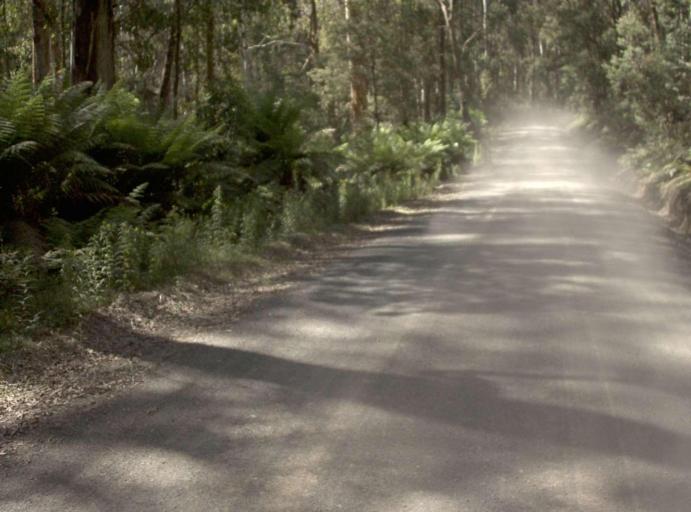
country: AU
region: New South Wales
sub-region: Bombala
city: Bombala
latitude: -37.2378
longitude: 148.7559
